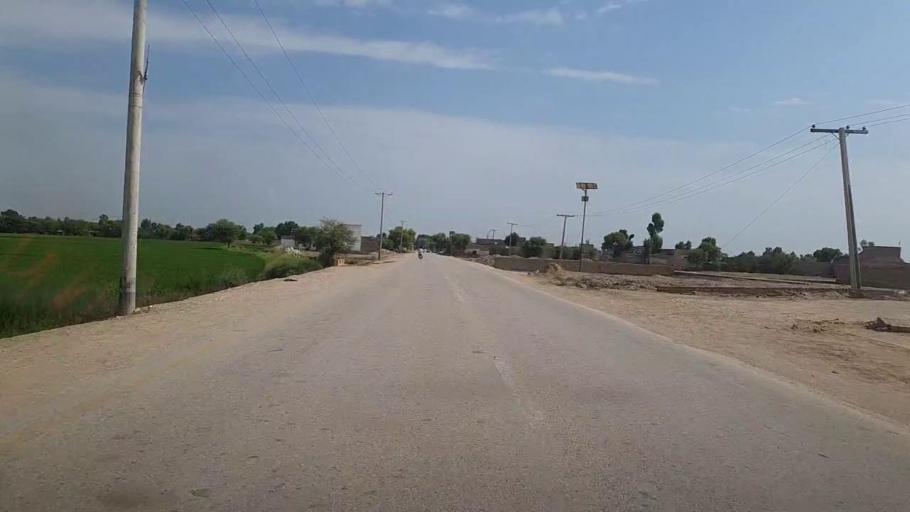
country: PK
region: Sindh
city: Thul
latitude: 28.2422
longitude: 68.7873
